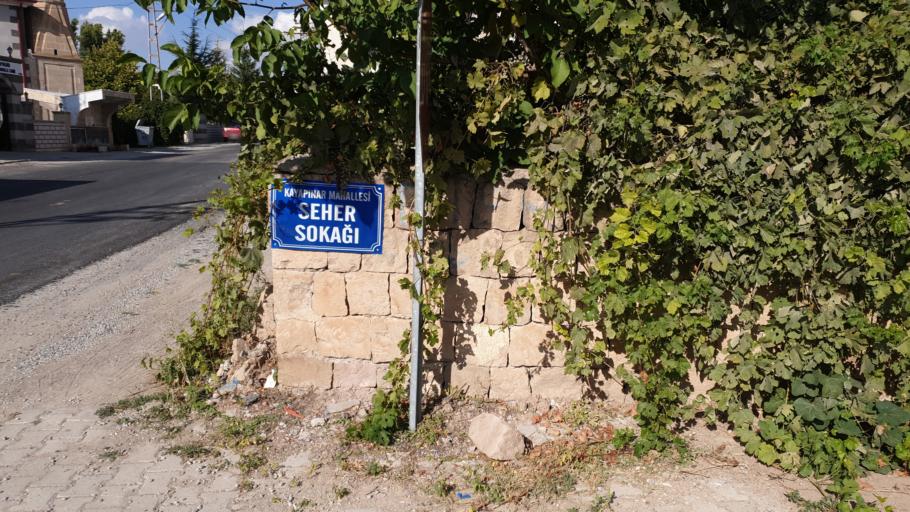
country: TR
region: Kayseri
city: Felahiye
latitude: 39.1157
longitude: 35.6137
